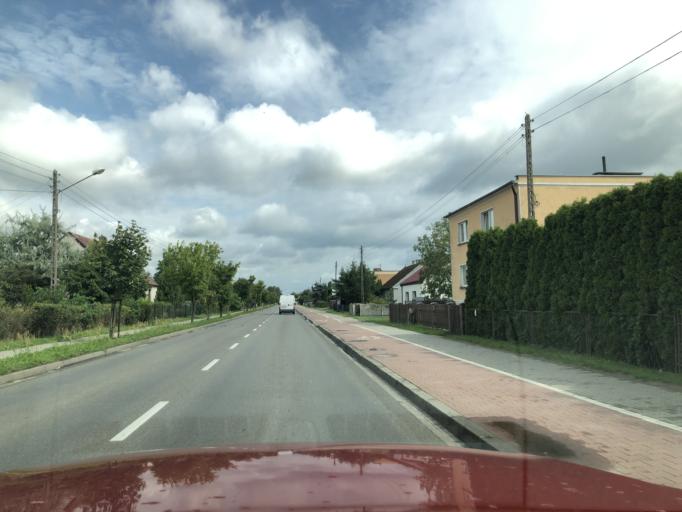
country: PL
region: Greater Poland Voivodeship
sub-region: Powiat szamotulski
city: Pniewy
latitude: 52.5163
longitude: 16.2611
